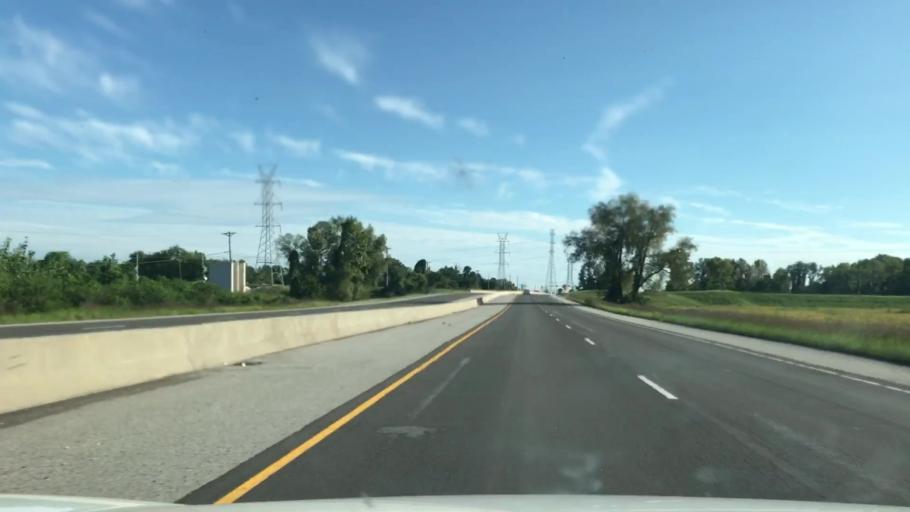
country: US
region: Illinois
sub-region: Madison County
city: Hartford
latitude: 38.8086
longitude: -90.0989
